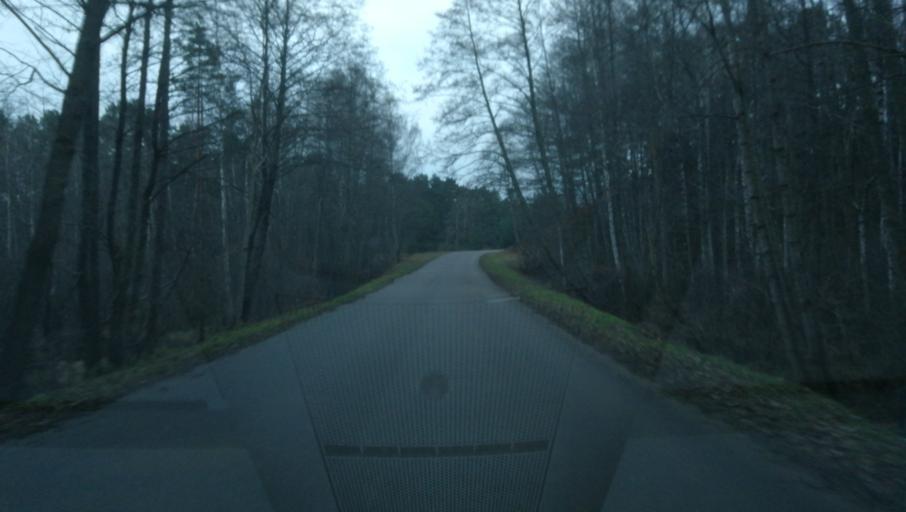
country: LV
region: Carnikava
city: Carnikava
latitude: 57.1455
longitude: 24.2927
